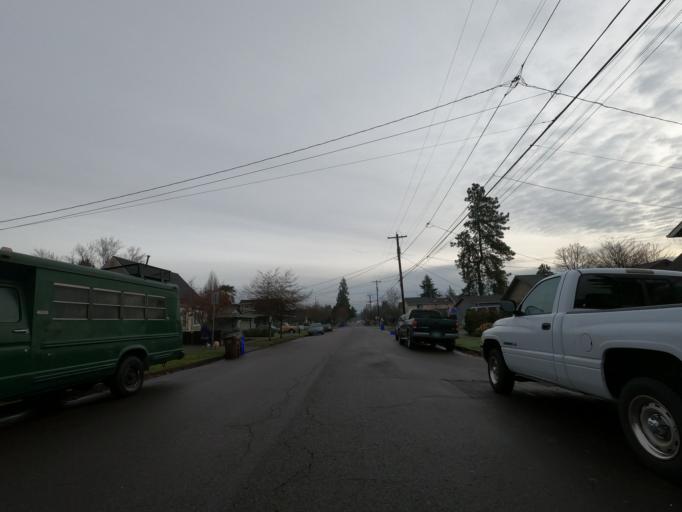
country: US
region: Oregon
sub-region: Clackamas County
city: Gladstone
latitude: 45.3788
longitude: -122.5967
